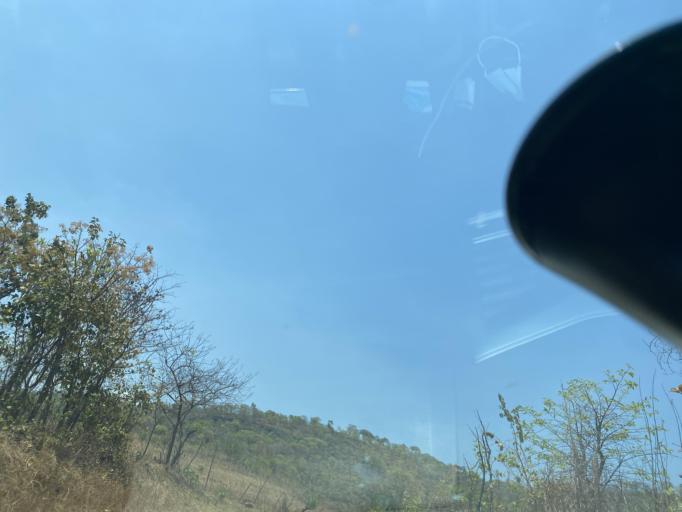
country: ZM
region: Lusaka
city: Kafue
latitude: -15.8071
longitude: 28.4335
